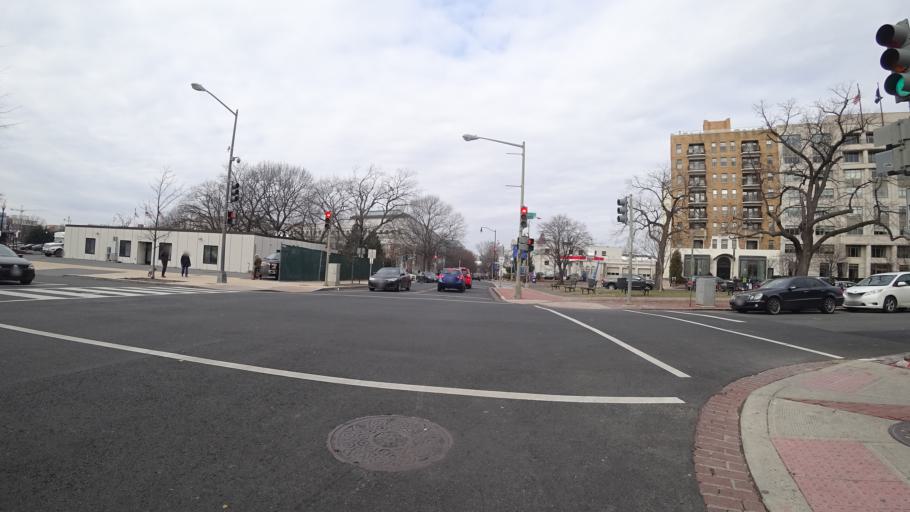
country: US
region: Washington, D.C.
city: Washington, D.C.
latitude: 38.8947
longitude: -77.0035
